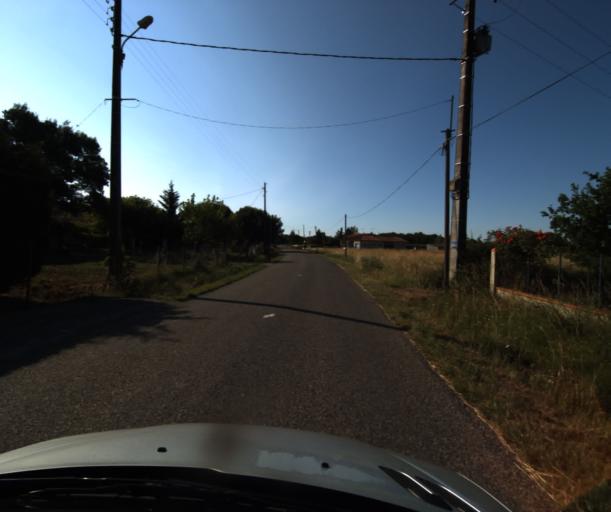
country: FR
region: Midi-Pyrenees
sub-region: Departement du Tarn-et-Garonne
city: Lafrancaise
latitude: 44.0732
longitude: 1.1958
